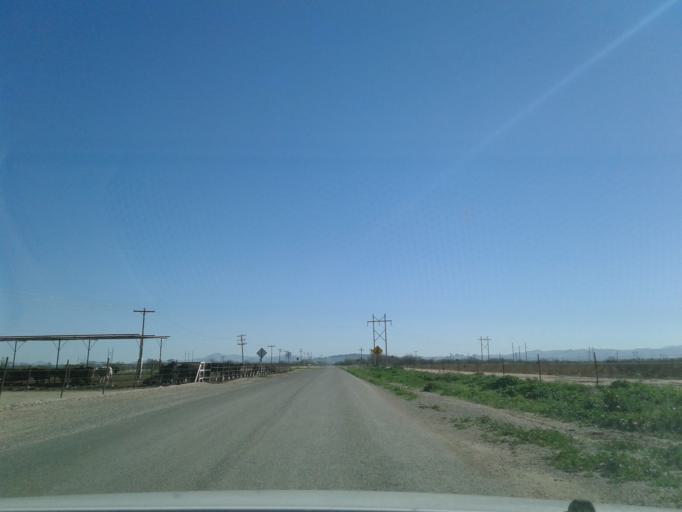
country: US
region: Arizona
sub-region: Pima County
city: Avra Valley
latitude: 32.5587
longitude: -111.3686
